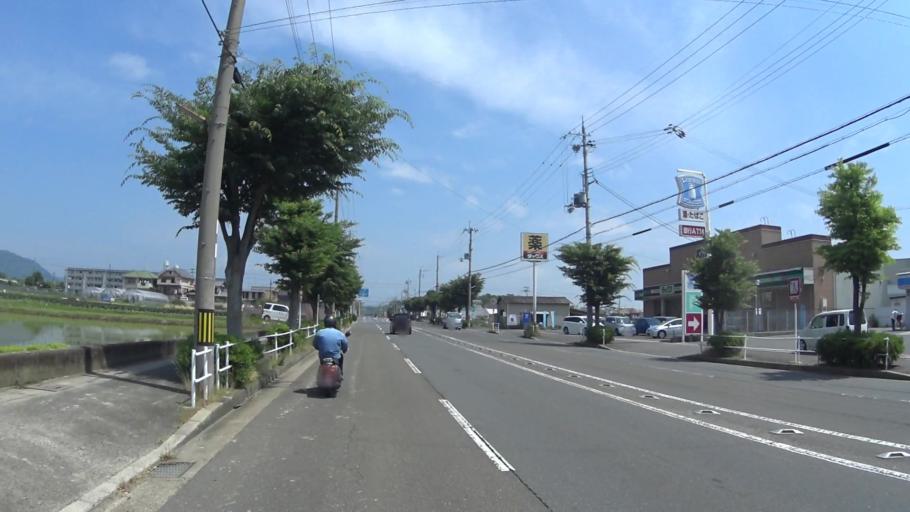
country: JP
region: Kyoto
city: Muko
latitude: 34.9372
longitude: 135.6859
